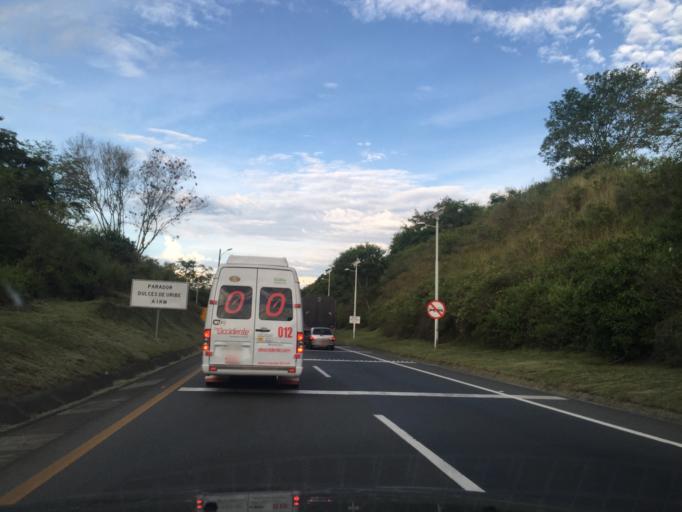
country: CO
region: Valle del Cauca
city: Bugalagrande
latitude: 4.2505
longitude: -76.1188
